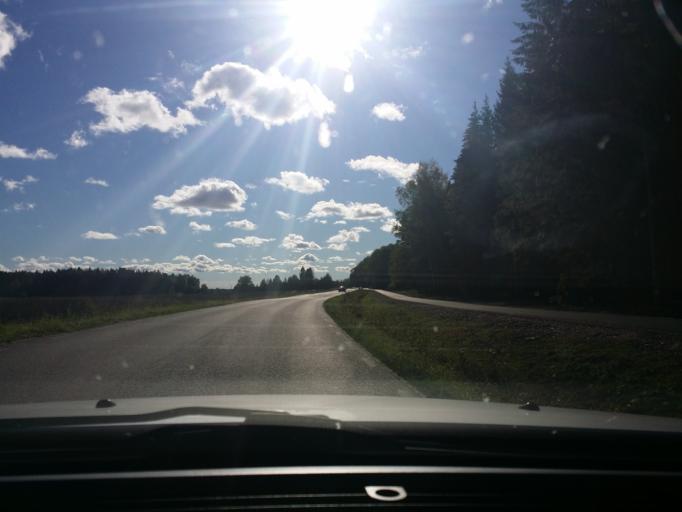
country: SE
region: Vaestmanland
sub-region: Vasteras
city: Vasteras
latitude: 59.5697
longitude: 16.4861
